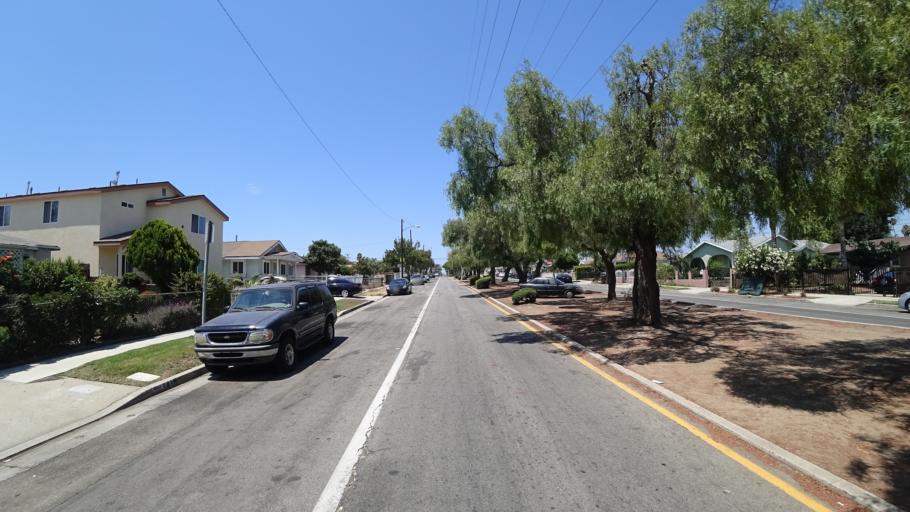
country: US
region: California
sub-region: Los Angeles County
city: Westmont
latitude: 33.9468
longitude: -118.3011
